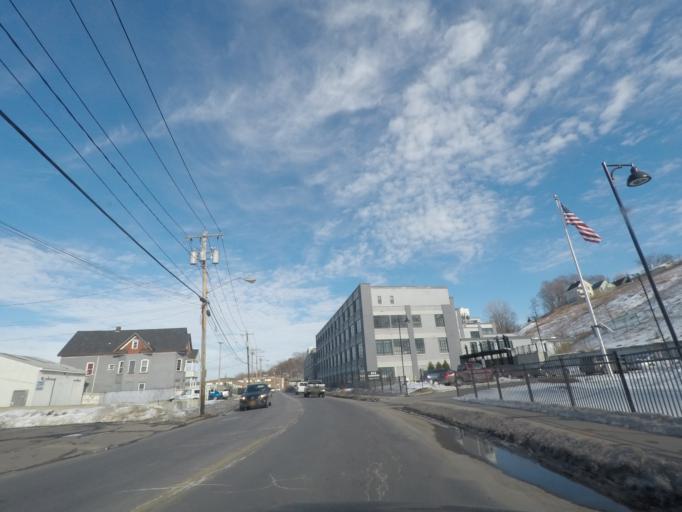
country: US
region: New York
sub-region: Schenectady County
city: Schenectady
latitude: 42.8033
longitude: -73.9529
